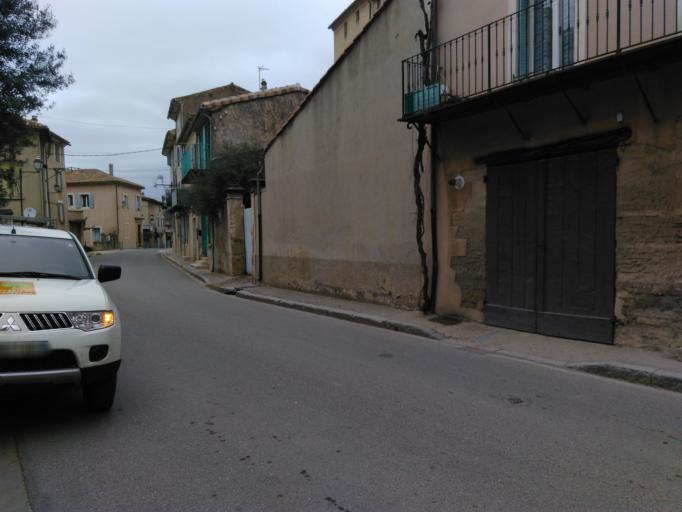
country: FR
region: Provence-Alpes-Cote d'Azur
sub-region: Departement du Vaucluse
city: Malemort-du-Comtat
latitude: 44.0208
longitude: 5.1590
